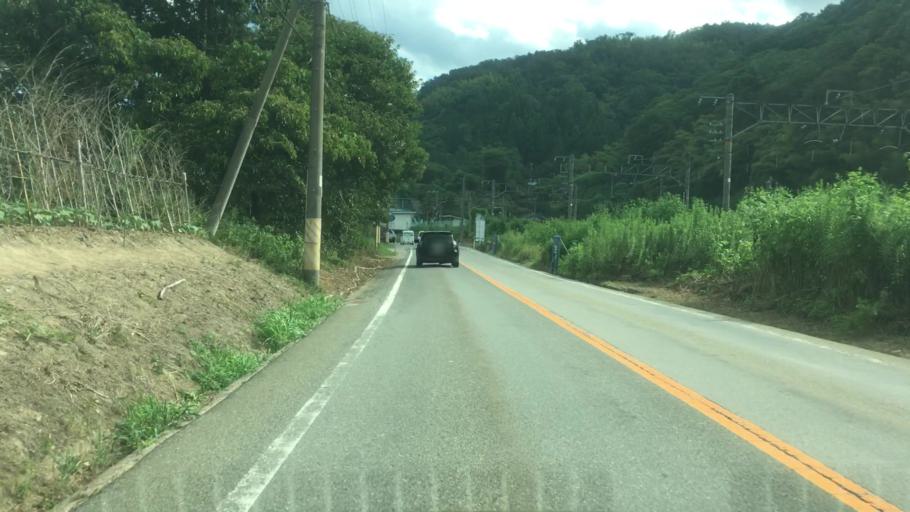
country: JP
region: Hyogo
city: Toyooka
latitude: 35.5905
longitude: 134.7994
